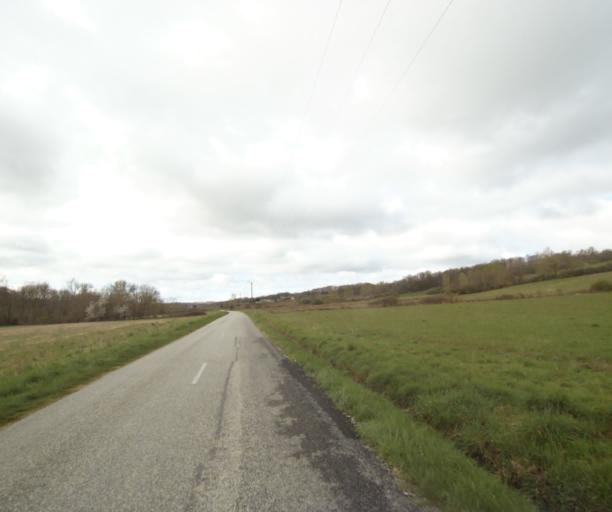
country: FR
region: Midi-Pyrenees
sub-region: Departement de l'Ariege
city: Saverdun
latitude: 43.2237
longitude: 1.5343
